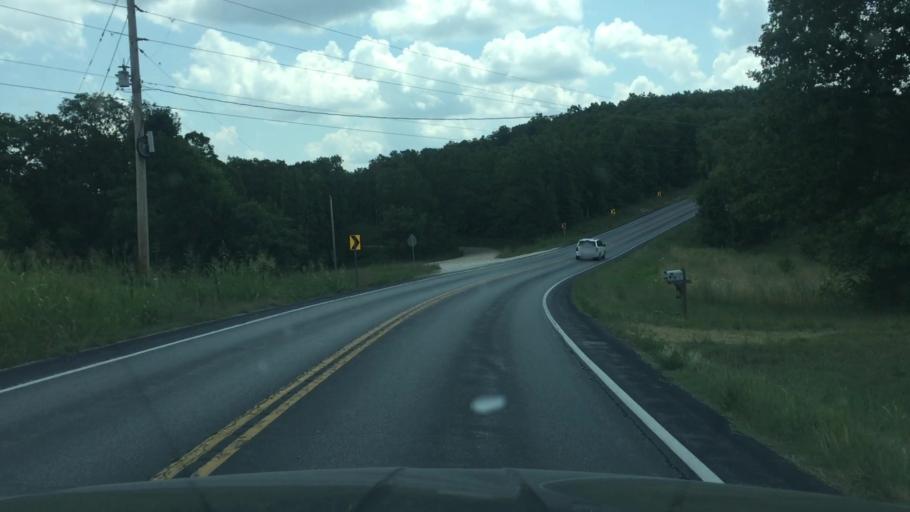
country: US
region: Missouri
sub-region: Miller County
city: Tuscumbia
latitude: 38.0997
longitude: -92.4968
